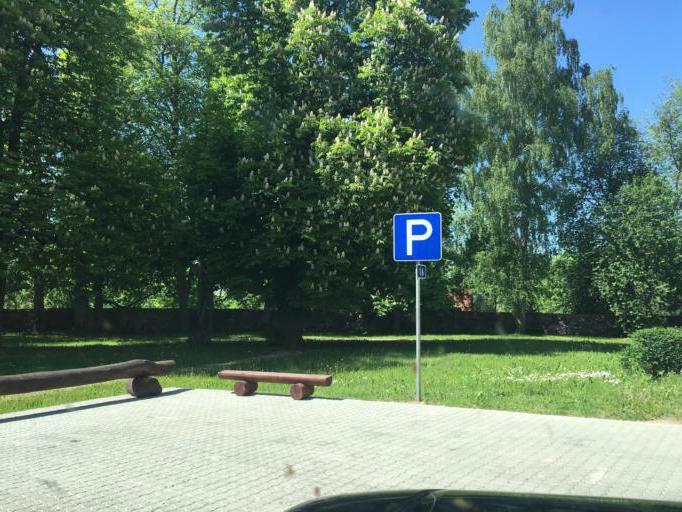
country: LV
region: Talsu Rajons
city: Valdemarpils
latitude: 57.4498
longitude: 22.5258
